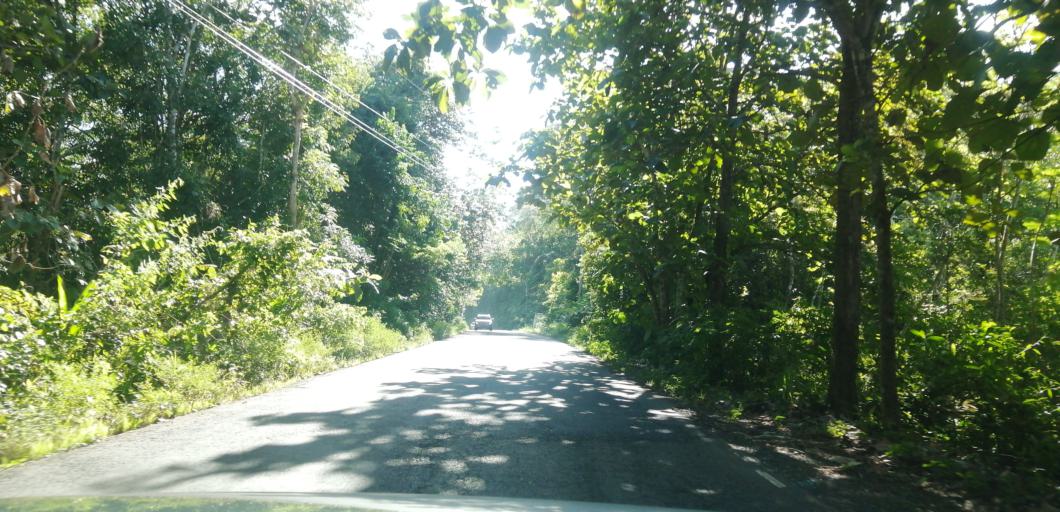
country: PA
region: Panama
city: Canita
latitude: 9.2061
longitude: -78.8269
